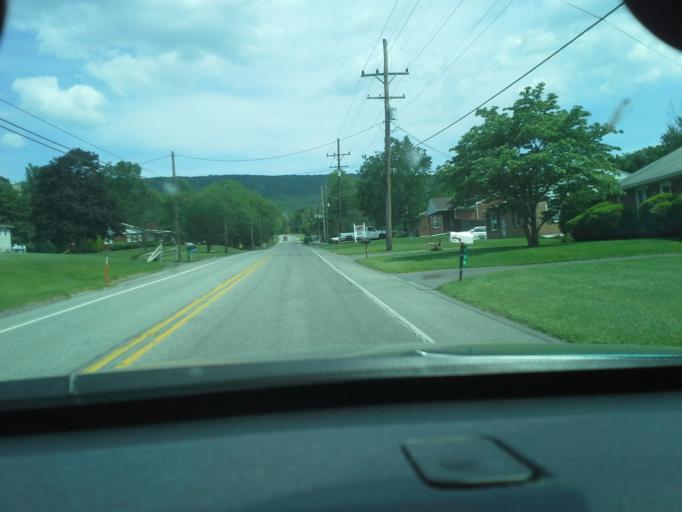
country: US
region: Pennsylvania
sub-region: Fulton County
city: McConnellsburg
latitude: 39.9224
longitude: -77.9819
